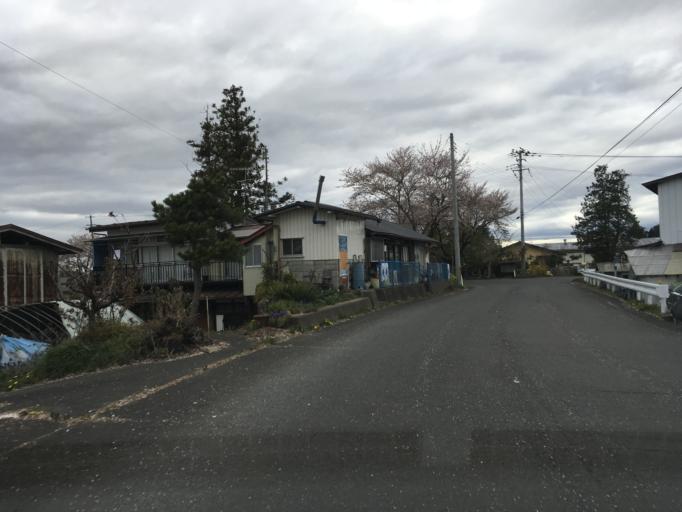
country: JP
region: Miyagi
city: Wakuya
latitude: 38.6422
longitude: 141.1872
